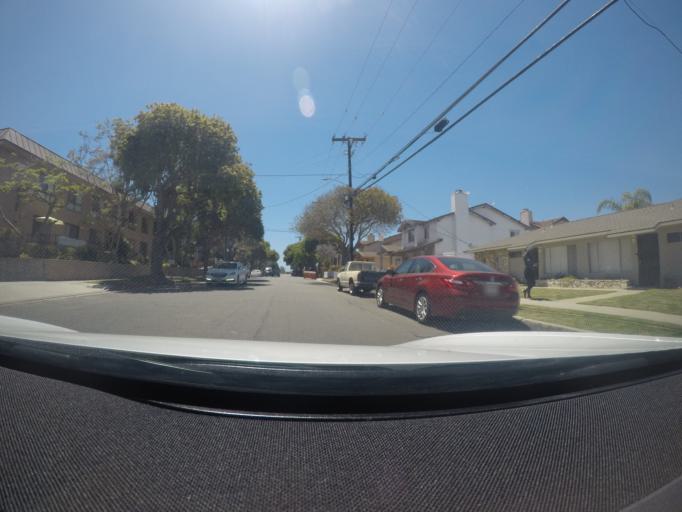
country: US
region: California
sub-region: Los Angeles County
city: Torrance
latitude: 33.8414
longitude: -118.3549
